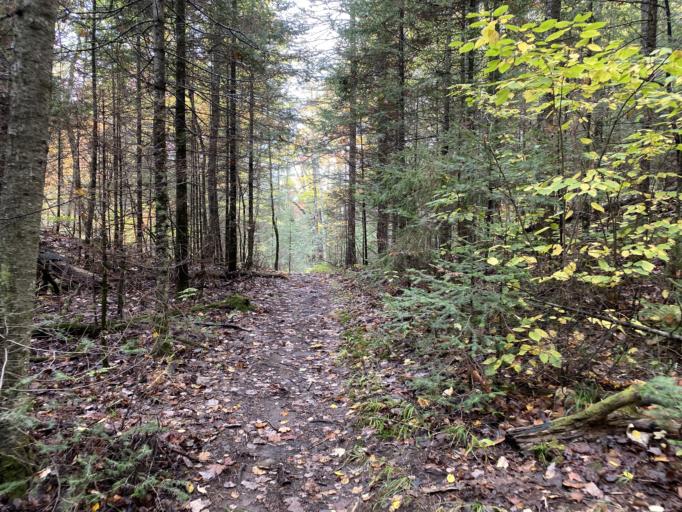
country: US
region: Michigan
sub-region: Marquette County
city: West Ishpeming
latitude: 46.5394
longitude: -87.9999
